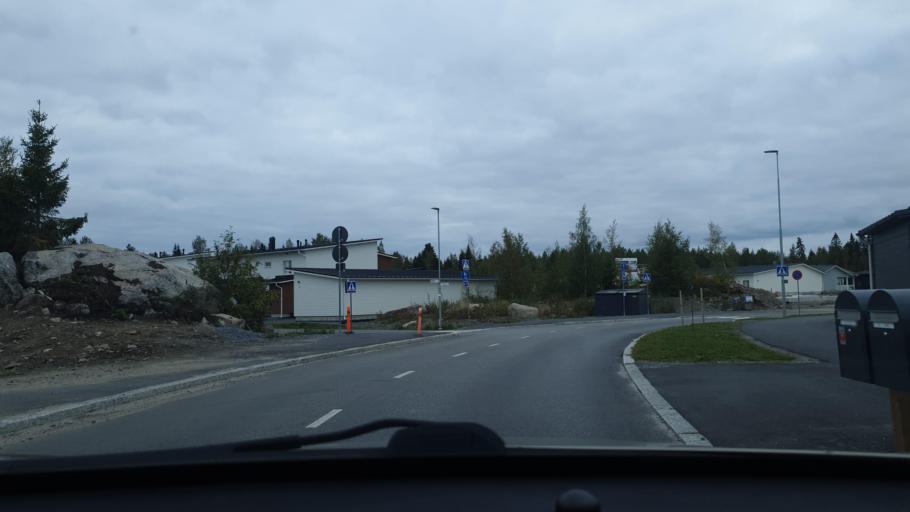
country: FI
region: Ostrobothnia
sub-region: Vaasa
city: Korsholm
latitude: 63.1278
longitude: 21.6563
